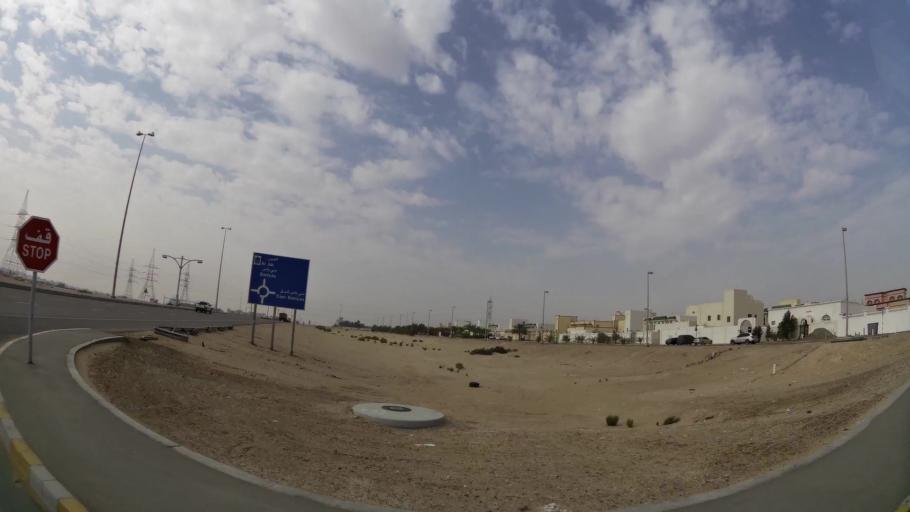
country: AE
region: Abu Dhabi
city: Abu Dhabi
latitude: 24.2991
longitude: 54.6641
